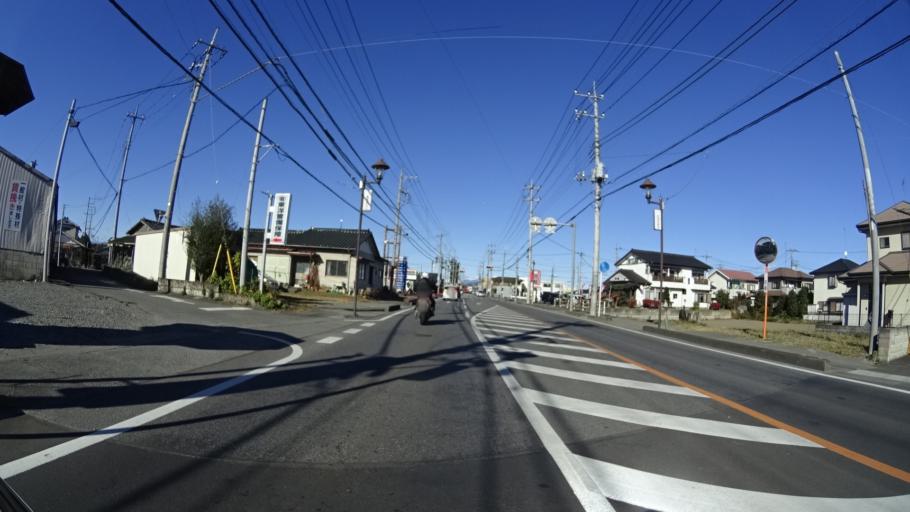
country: JP
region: Tochigi
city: Kanuma
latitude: 36.5116
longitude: 139.7516
